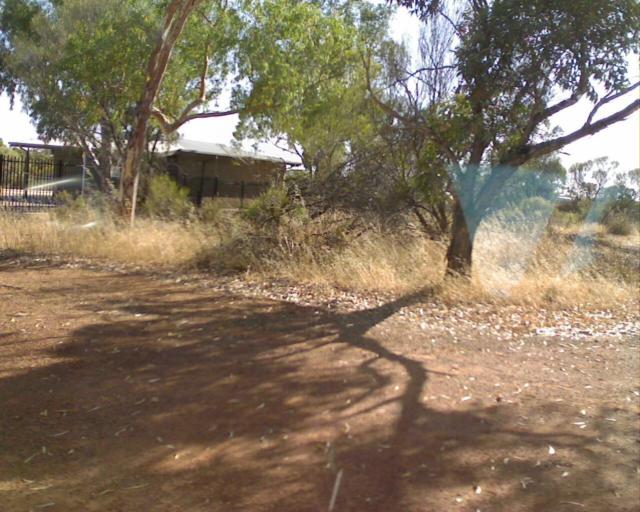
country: AU
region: Western Australia
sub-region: Wongan-Ballidu
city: Wongan Hills
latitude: -30.2821
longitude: 116.6580
